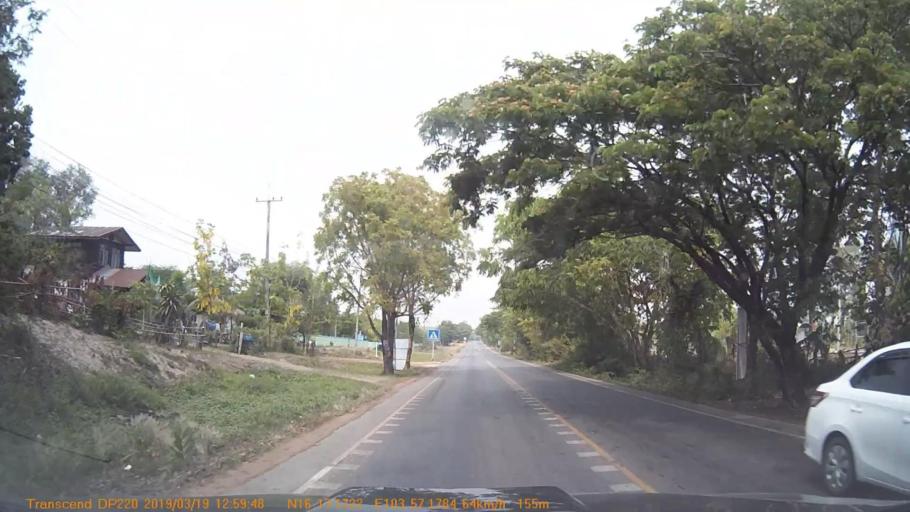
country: TH
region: Roi Et
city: Waeng
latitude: 16.2200
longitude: 103.9531
